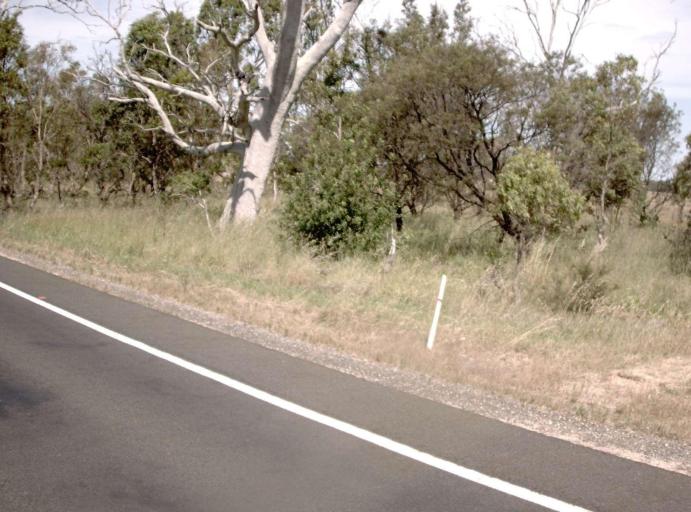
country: AU
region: Victoria
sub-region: East Gippsland
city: Bairnsdale
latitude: -37.8683
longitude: 147.4801
